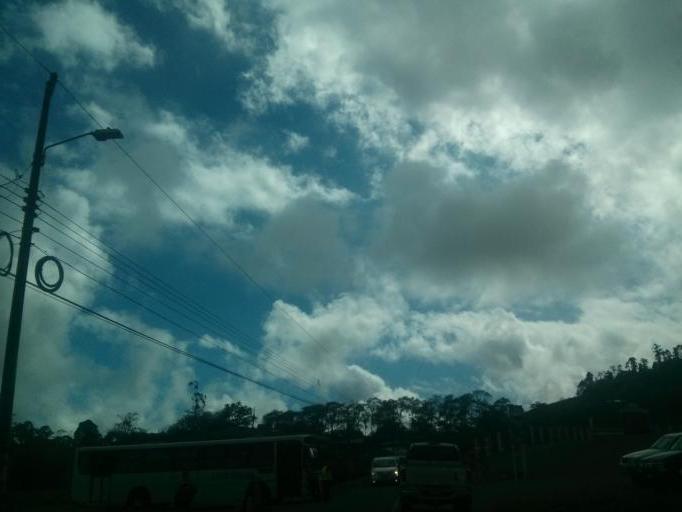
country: CR
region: Cartago
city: Turrialba
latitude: 9.9438
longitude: -83.7757
